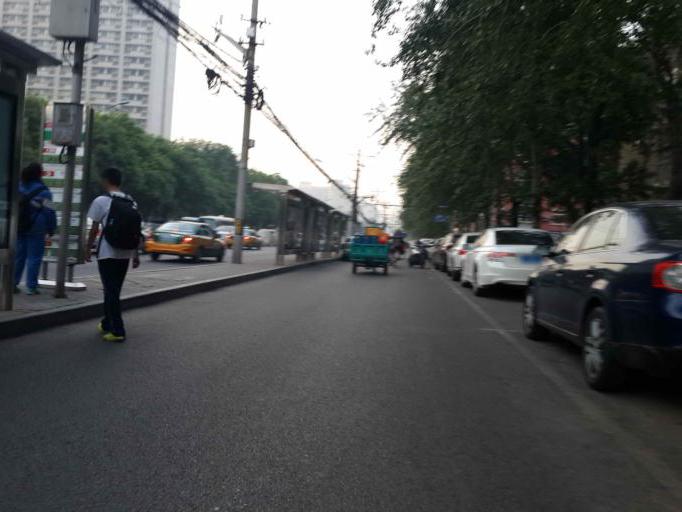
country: CN
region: Beijing
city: Chaowai
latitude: 39.9339
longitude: 116.4444
